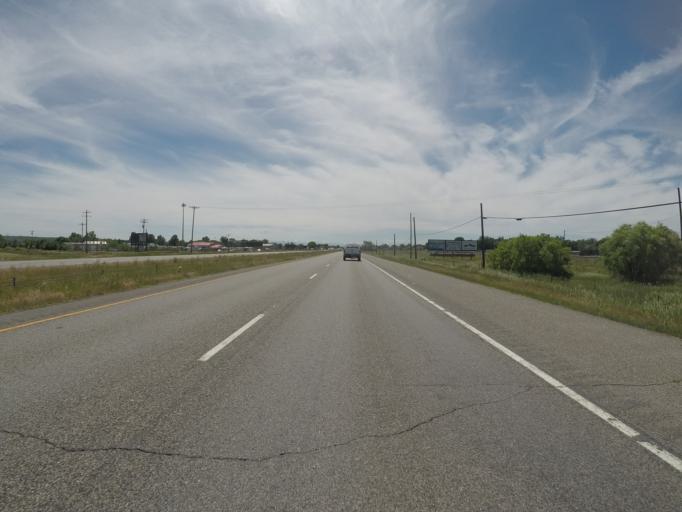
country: US
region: Montana
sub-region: Yellowstone County
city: Laurel
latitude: 45.7159
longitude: -108.6373
